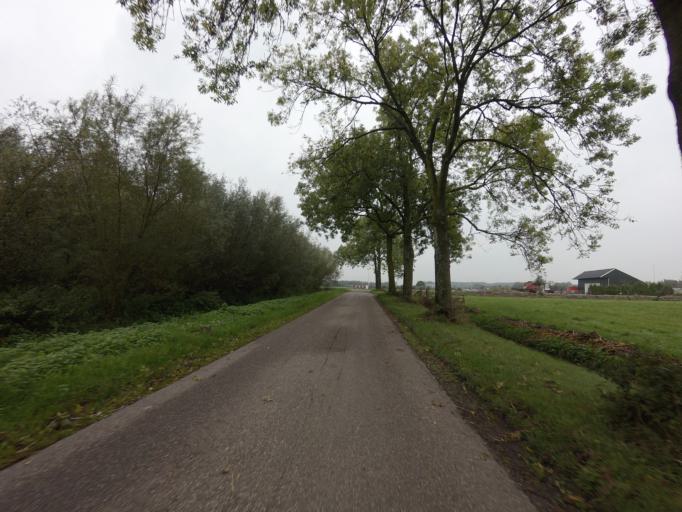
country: NL
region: Gelderland
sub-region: Gemeente Culemborg
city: Culemborg
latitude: 51.9199
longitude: 5.1701
